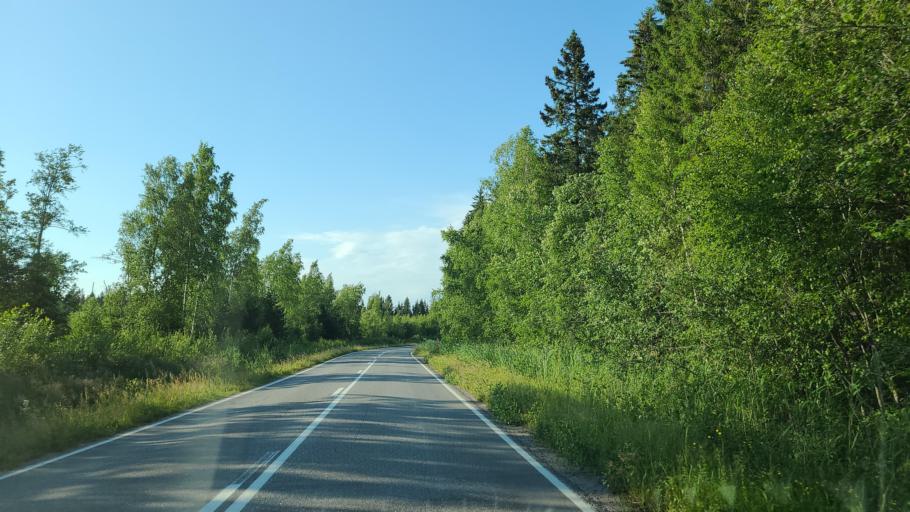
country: FI
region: Ostrobothnia
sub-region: Vaasa
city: Replot
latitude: 63.3024
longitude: 21.3585
